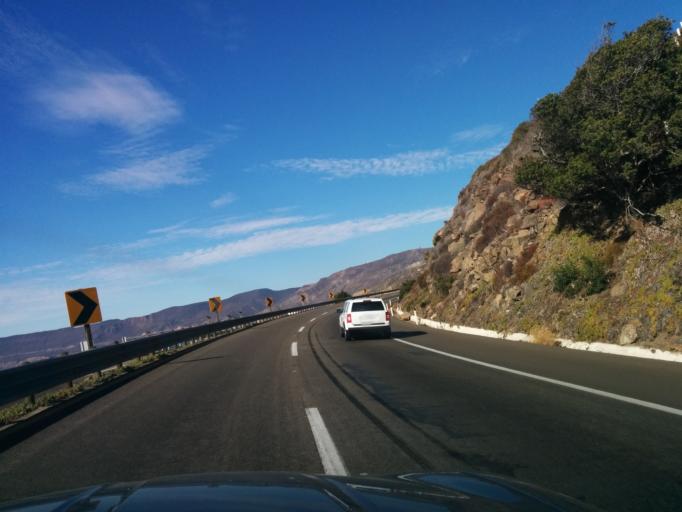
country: MX
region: Baja California
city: El Sauzal
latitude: 31.9316
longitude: -116.7540
